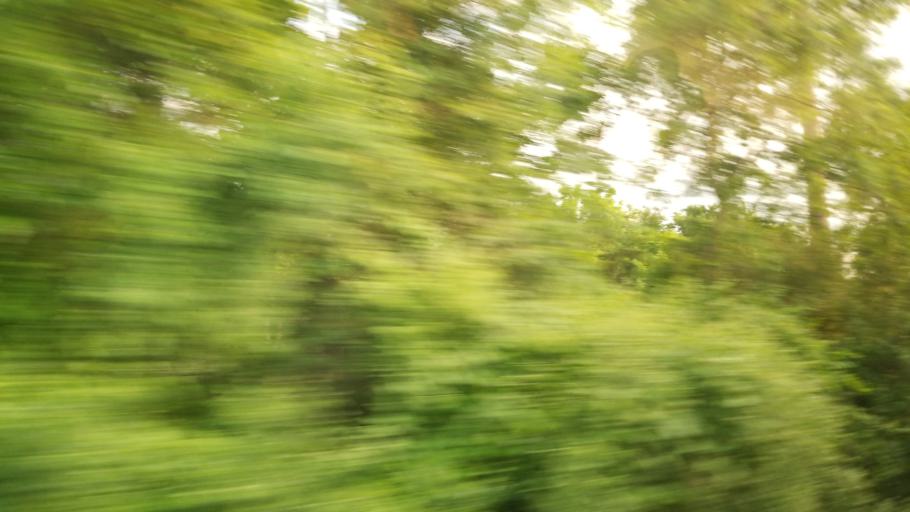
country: US
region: Virginia
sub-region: City of Manassas
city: Manassas
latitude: 38.7603
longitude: -77.4486
